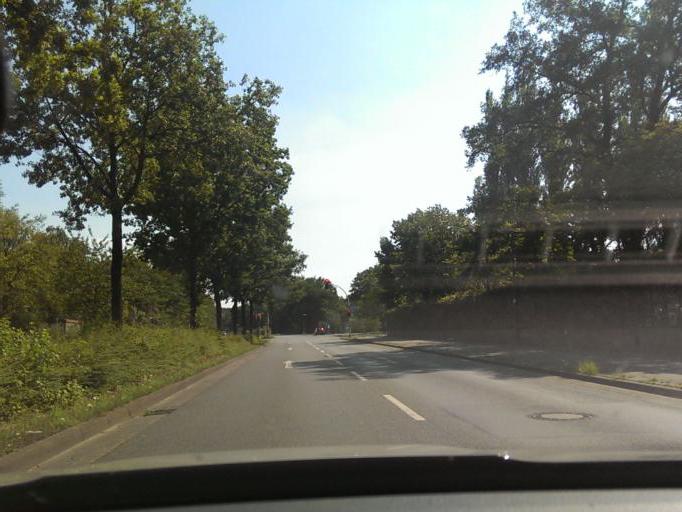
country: DE
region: Lower Saxony
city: Langenhagen
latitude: 52.4342
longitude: 9.7582
